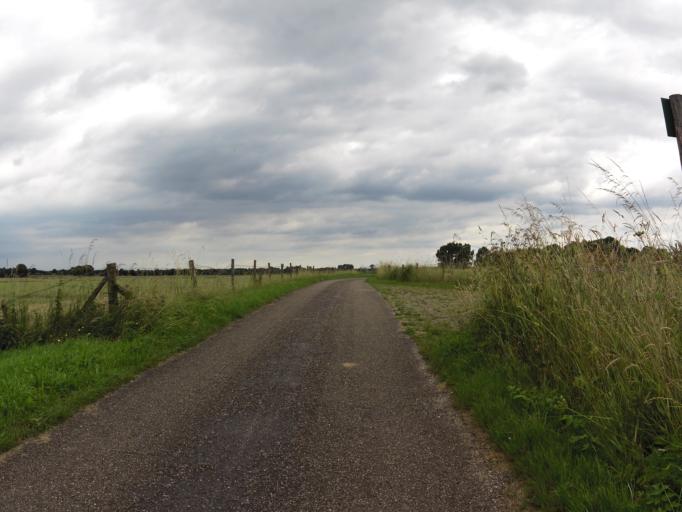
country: NL
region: North Brabant
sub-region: Gemeente Landerd
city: Reek
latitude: 51.7716
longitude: 5.6852
